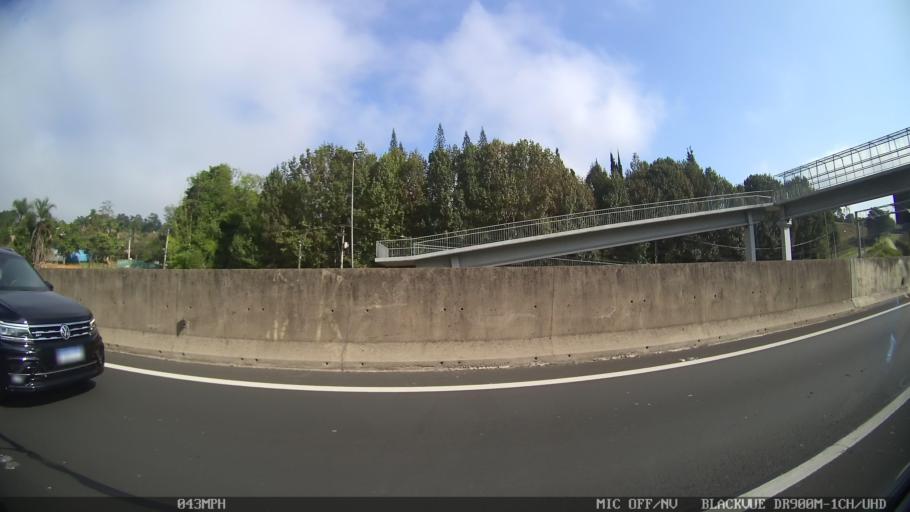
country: BR
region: Sao Paulo
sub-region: Varzea Paulista
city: Varzea Paulista
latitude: -23.2558
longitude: -46.8681
